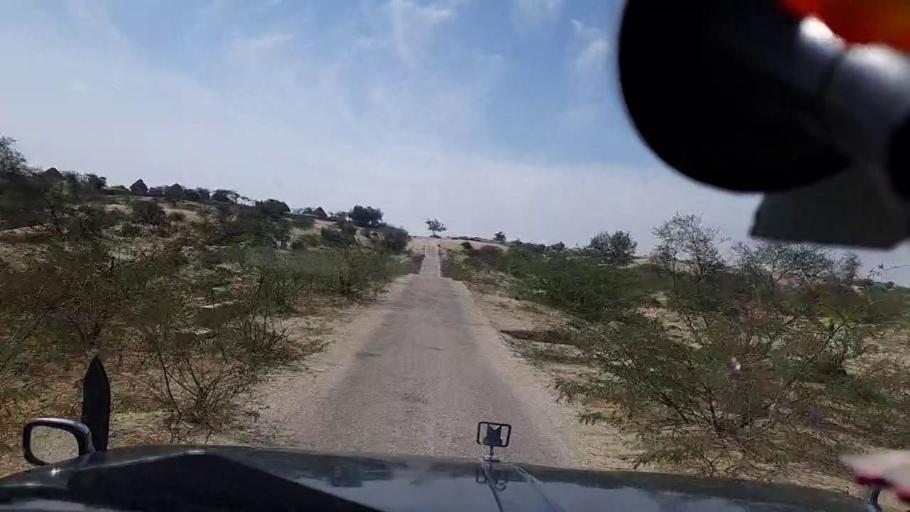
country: PK
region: Sindh
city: Diplo
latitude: 24.3726
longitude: 69.5839
